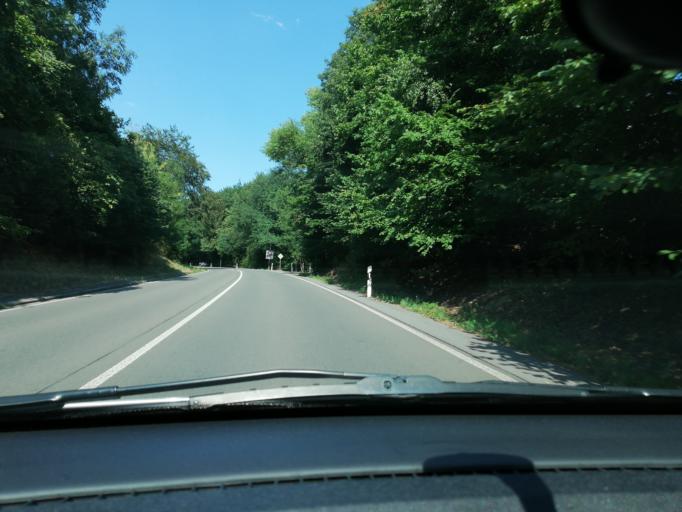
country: DE
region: North Rhine-Westphalia
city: Sprockhovel
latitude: 51.3822
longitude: 7.2988
